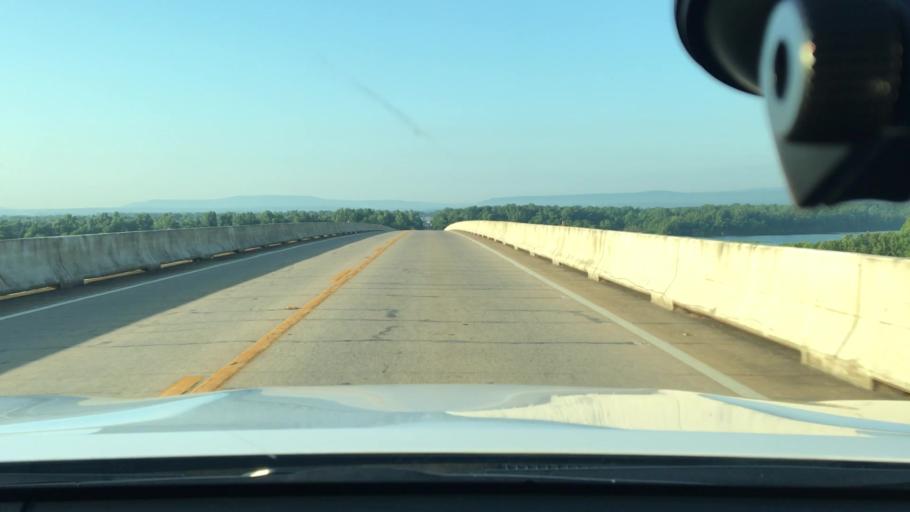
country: US
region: Arkansas
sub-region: Johnson County
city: Clarksville
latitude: 35.4123
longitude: -93.5321
